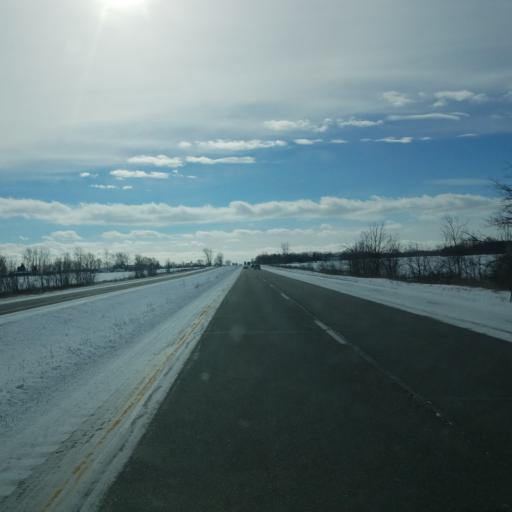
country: US
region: Michigan
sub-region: Gratiot County
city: Ithaca
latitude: 43.2377
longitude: -84.5634
